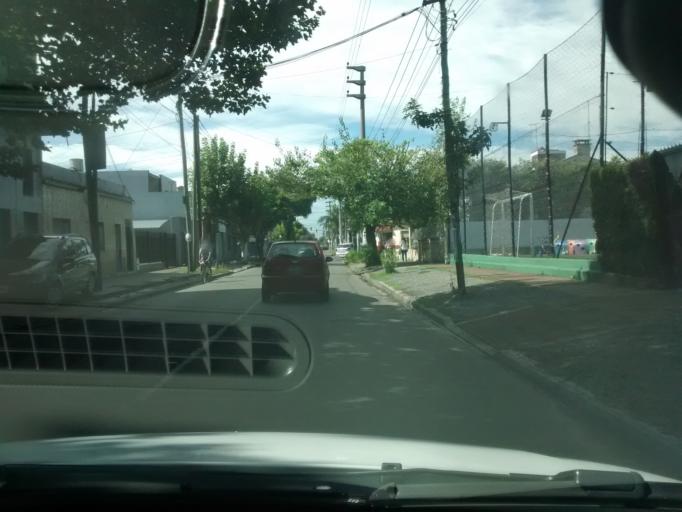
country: AR
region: Buenos Aires
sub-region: Partido de Moron
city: Moron
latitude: -34.6665
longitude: -58.6162
